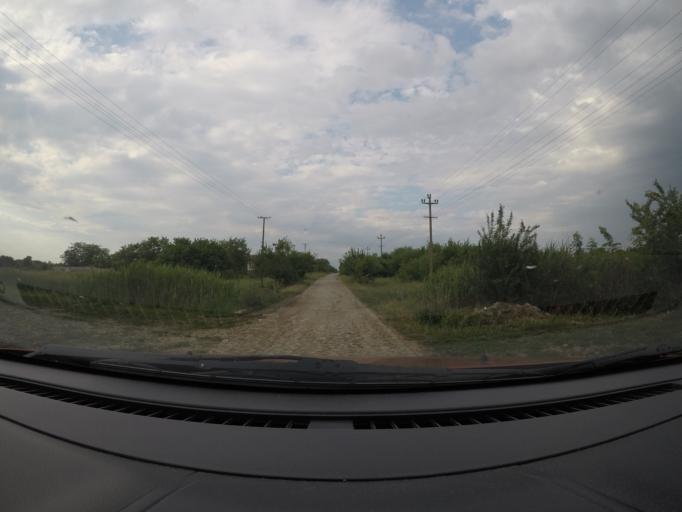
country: RS
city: Uzdin
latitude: 45.1999
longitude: 20.6114
